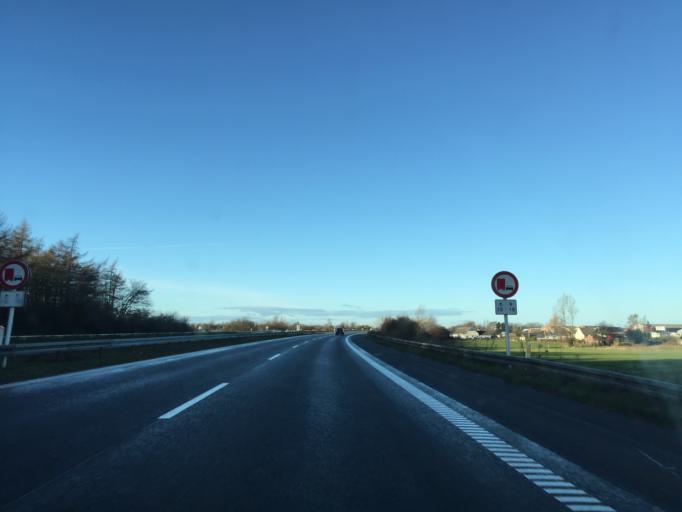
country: DK
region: South Denmark
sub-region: Middelfart Kommune
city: Norre Aby
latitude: 55.4652
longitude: 9.9046
